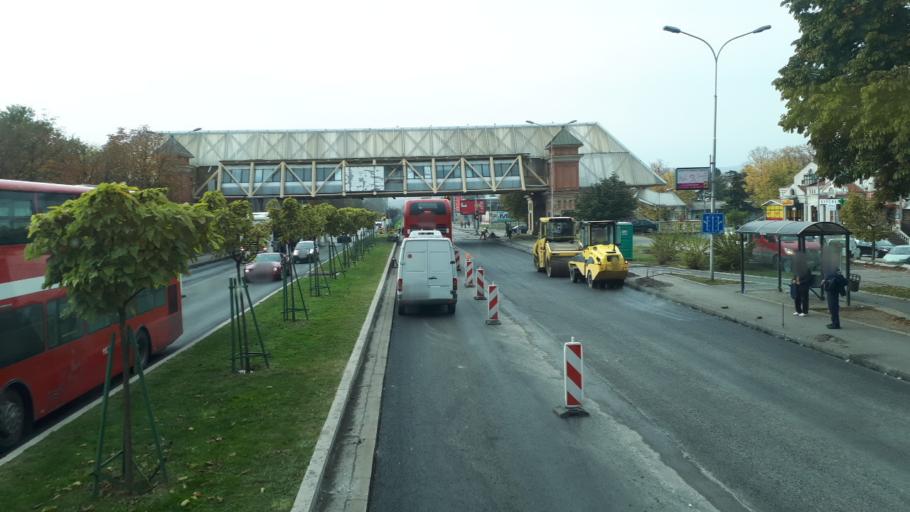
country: MK
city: Krushopek
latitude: 42.0066
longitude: 21.3764
